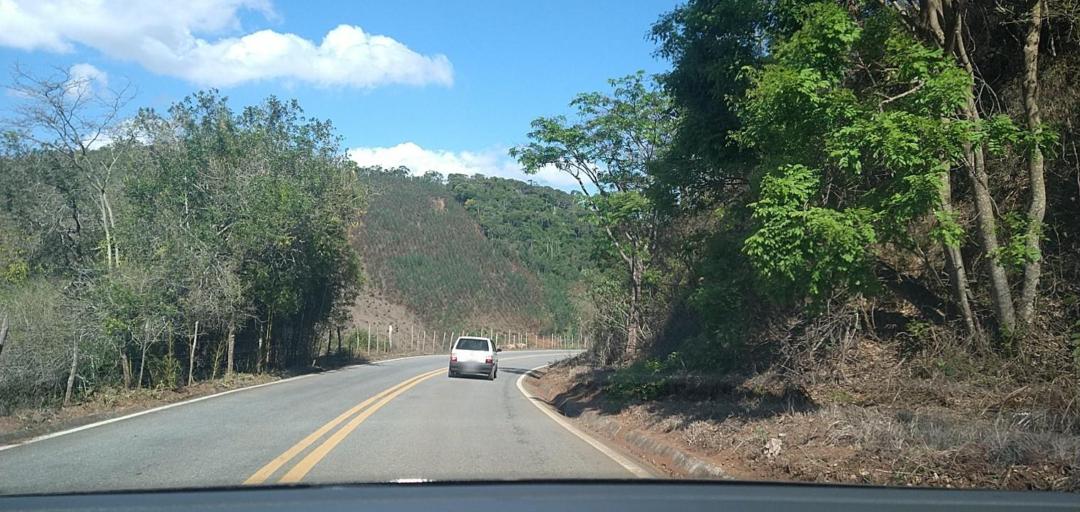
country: BR
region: Minas Gerais
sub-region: Alvinopolis
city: Alvinopolis
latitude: -20.0357
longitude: -43.0354
